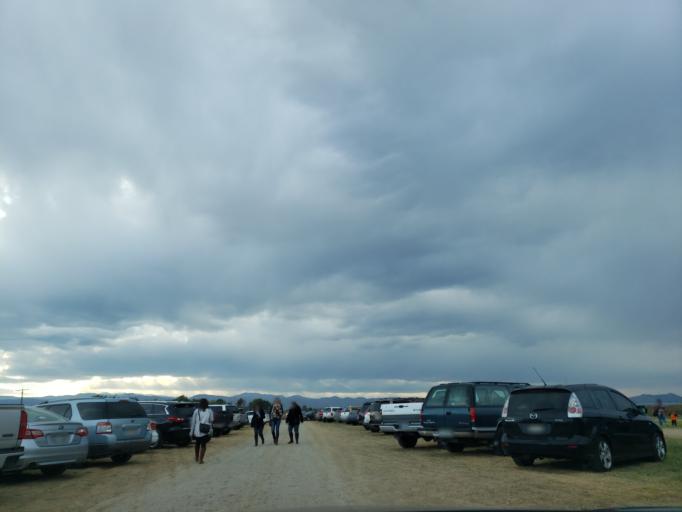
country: US
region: Colorado
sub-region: Larimer County
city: Wellington
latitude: 40.6395
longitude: -105.0137
